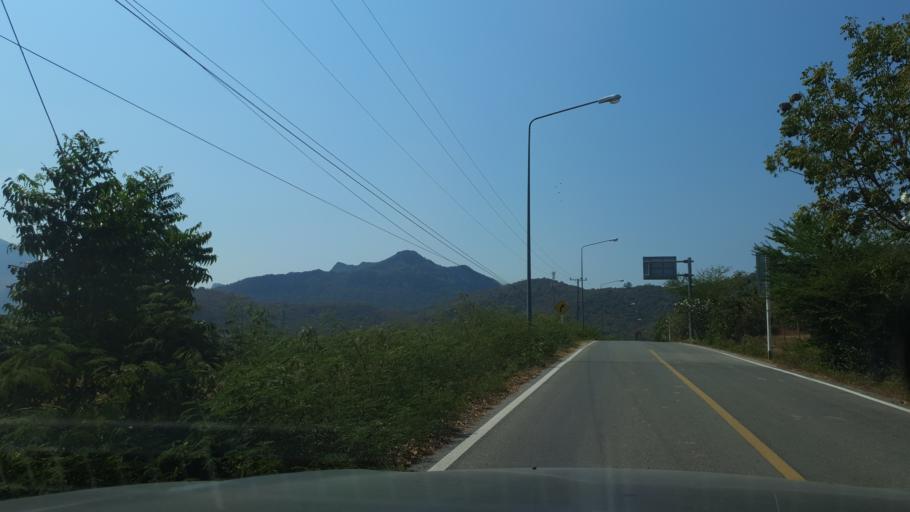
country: TH
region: Prachuap Khiri Khan
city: Sam Roi Yot
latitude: 12.2858
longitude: 99.9706
